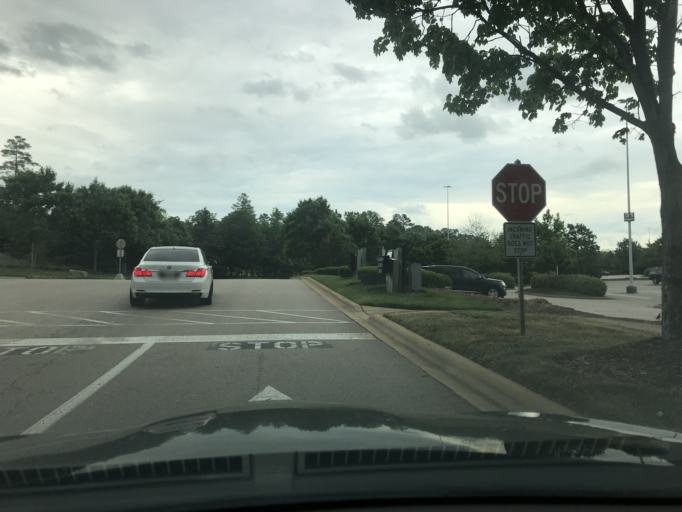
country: US
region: North Carolina
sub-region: Wake County
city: Raleigh
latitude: 35.8688
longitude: -78.5774
